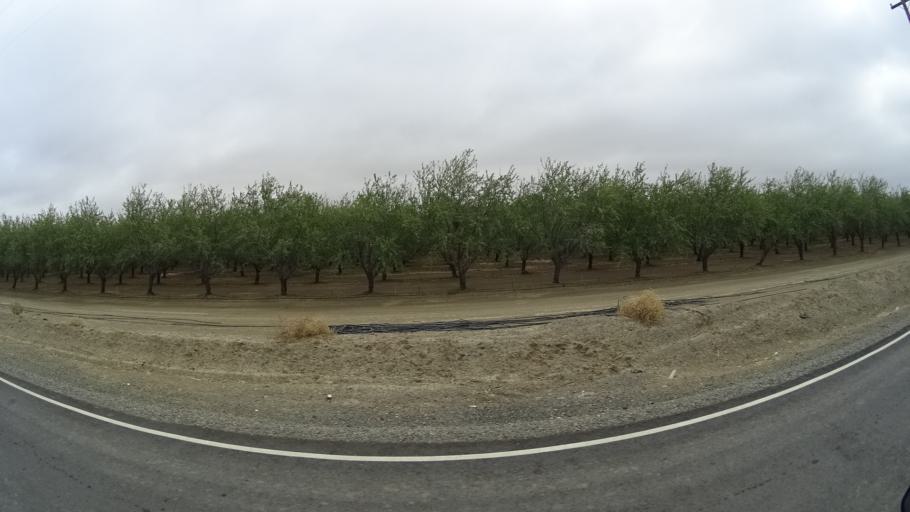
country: US
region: California
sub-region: Yolo County
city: Esparto
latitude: 38.7762
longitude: -122.0439
